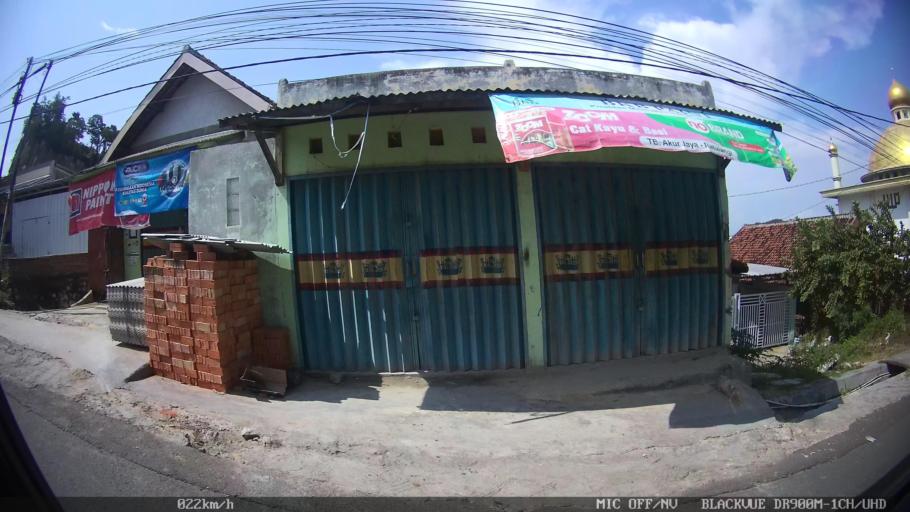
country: ID
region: Lampung
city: Kedaton
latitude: -5.3971
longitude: 105.2548
